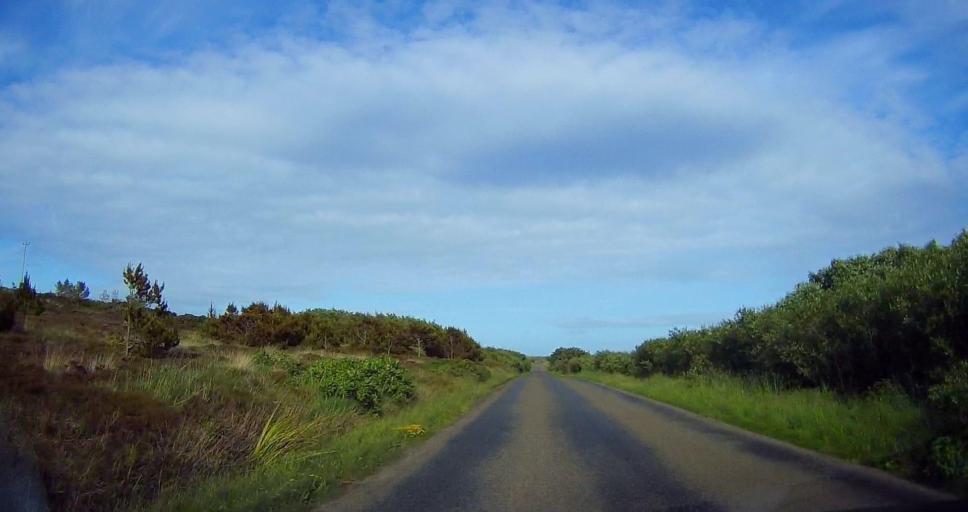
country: GB
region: Scotland
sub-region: Orkney Islands
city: Stromness
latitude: 58.8029
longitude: -3.2356
